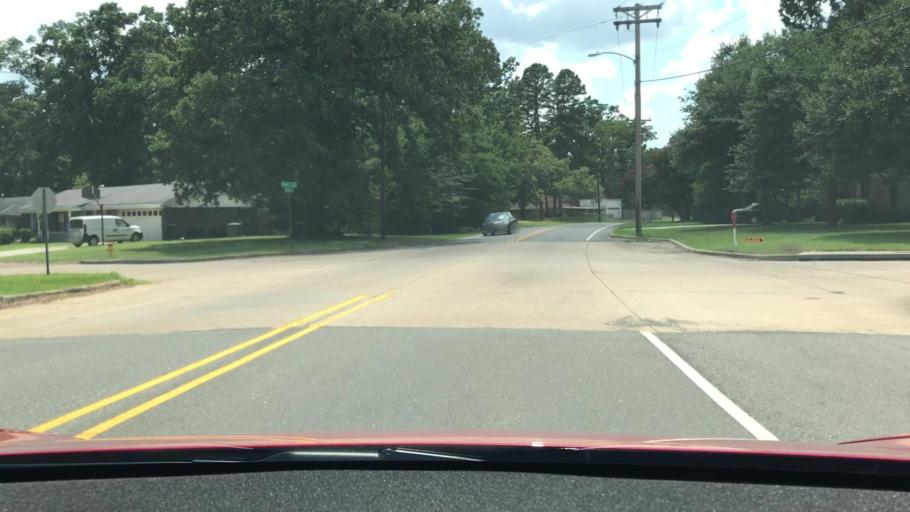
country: US
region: Louisiana
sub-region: De Soto Parish
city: Stonewall
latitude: 32.3897
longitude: -93.7859
